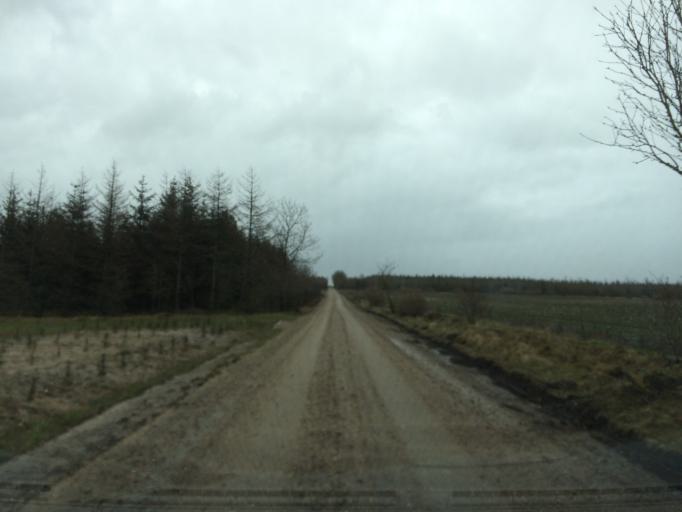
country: DK
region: Central Jutland
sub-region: Holstebro Kommune
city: Holstebro
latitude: 56.2227
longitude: 8.5049
